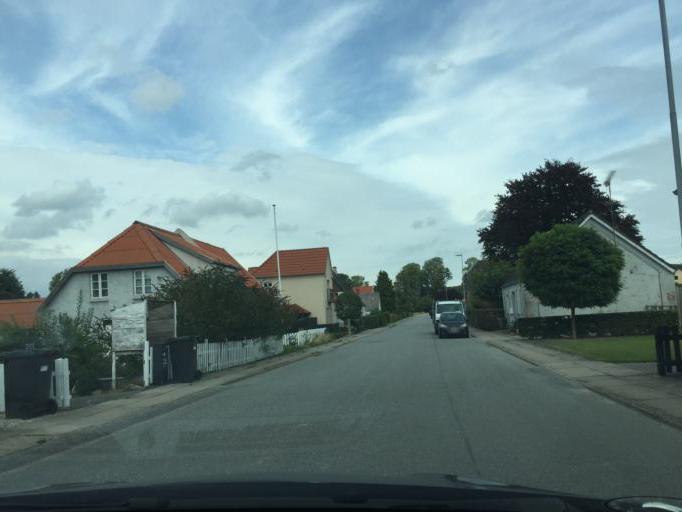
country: DK
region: South Denmark
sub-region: Assens Kommune
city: Vissenbjerg
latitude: 55.3656
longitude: 10.1452
